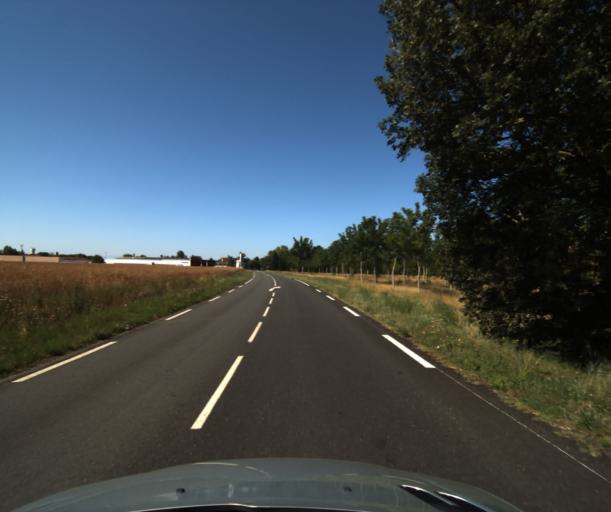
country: FR
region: Midi-Pyrenees
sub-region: Departement de la Haute-Garonne
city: Roquettes
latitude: 43.5041
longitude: 1.3736
